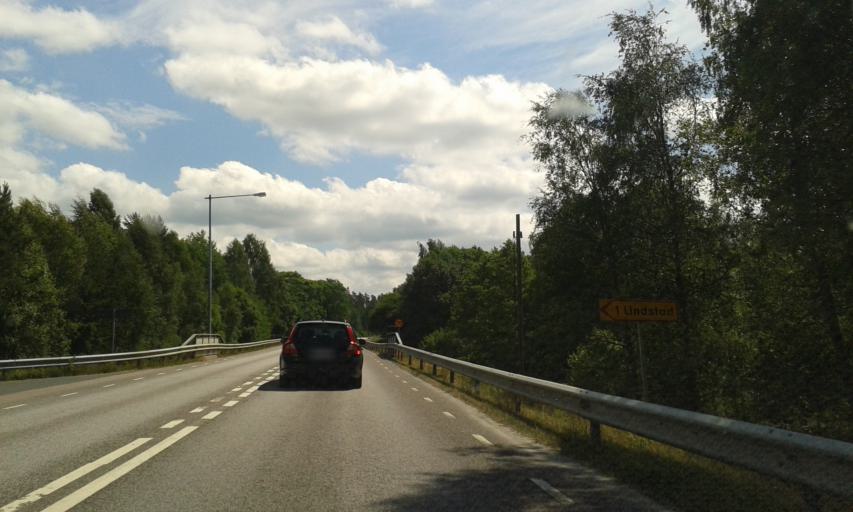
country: SE
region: Joenkoeping
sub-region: Varnamo Kommun
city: Rydaholm
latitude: 56.9710
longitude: 14.3282
